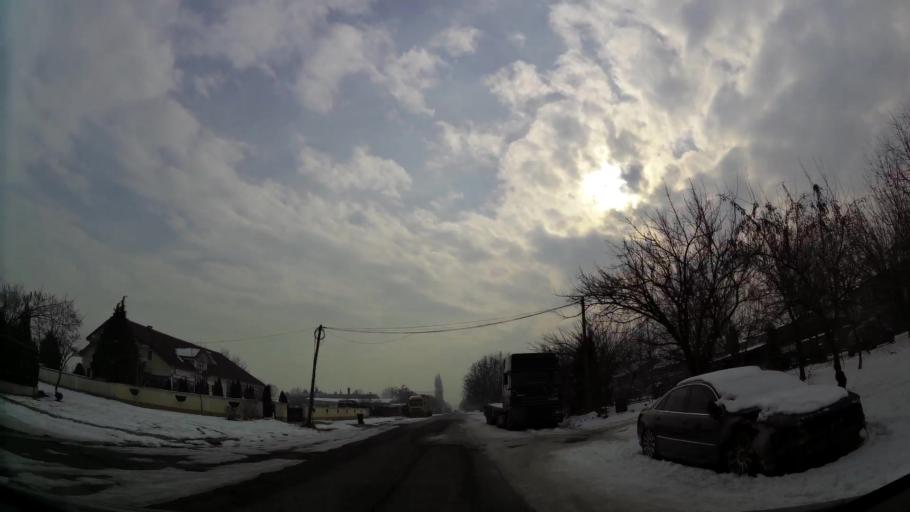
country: MK
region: Saraj
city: Saraj
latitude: 42.0224
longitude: 21.3569
